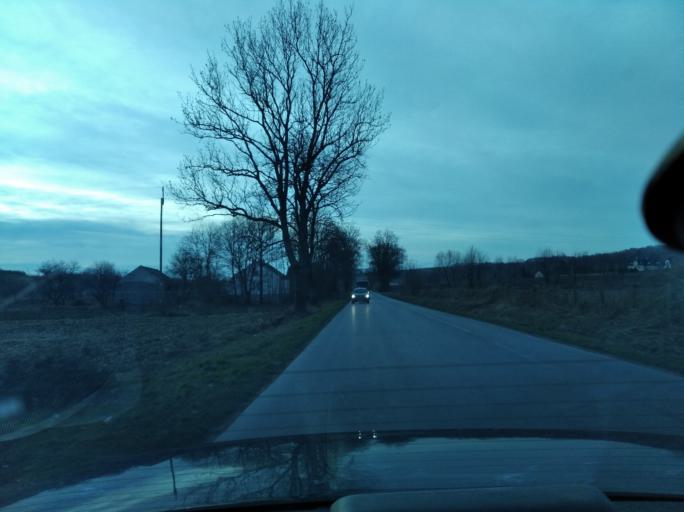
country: PL
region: Subcarpathian Voivodeship
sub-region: Powiat ropczycko-sedziszowski
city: Iwierzyce
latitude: 50.0409
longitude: 21.7454
